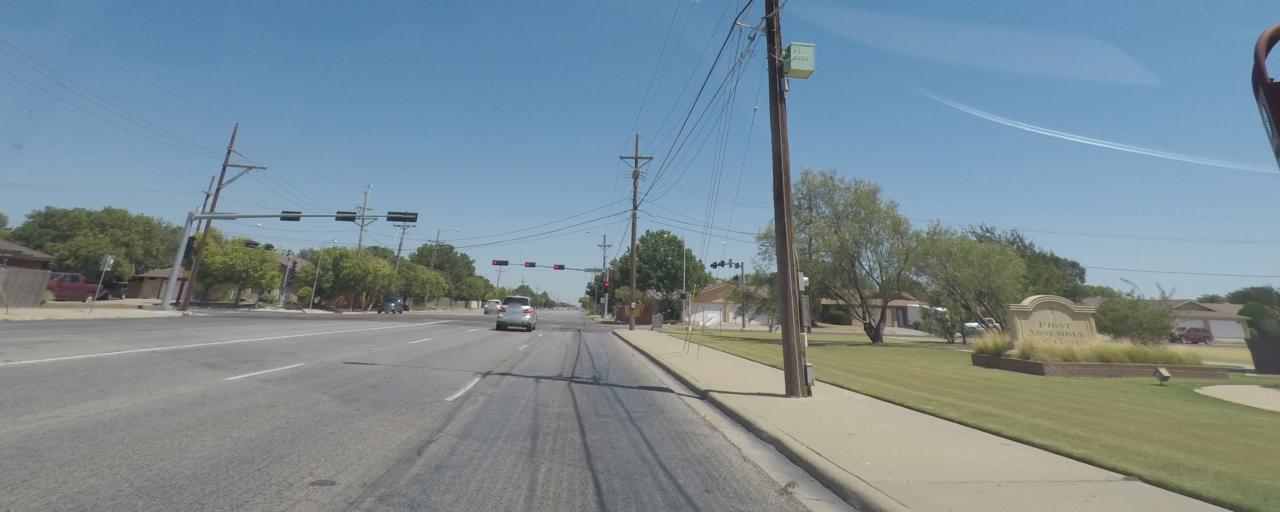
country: US
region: Texas
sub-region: Lubbock County
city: Lubbock
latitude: 33.5052
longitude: -101.8972
